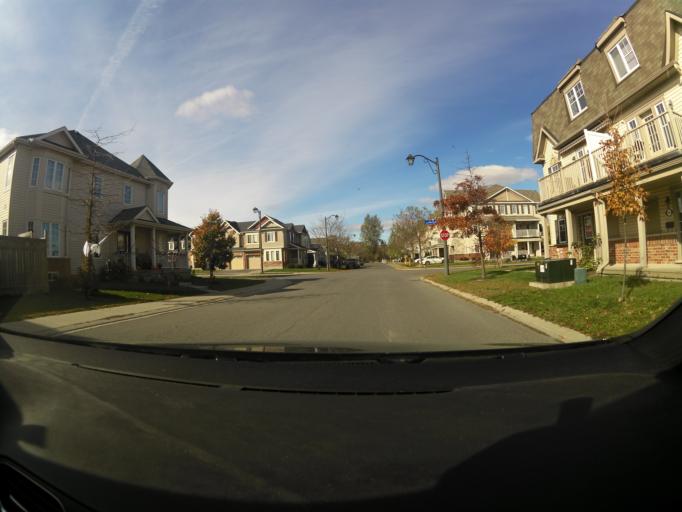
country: CA
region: Ontario
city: Bells Corners
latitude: 45.2880
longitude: -75.9243
